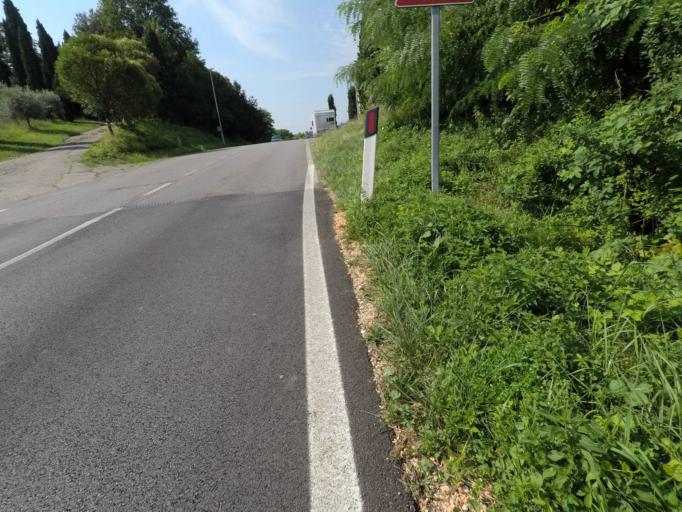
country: IT
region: Veneto
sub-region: Provincia di Treviso
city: Conegliano
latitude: 45.9028
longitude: 12.3013
